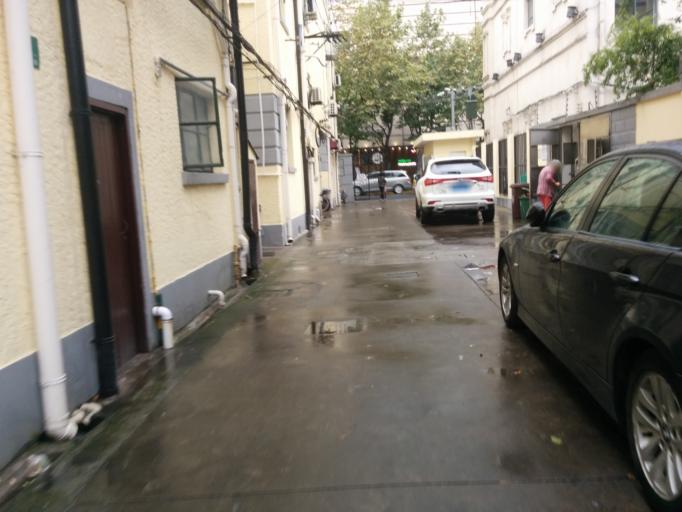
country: CN
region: Shanghai Shi
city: Shanghai
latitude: 31.2262
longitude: 121.4466
